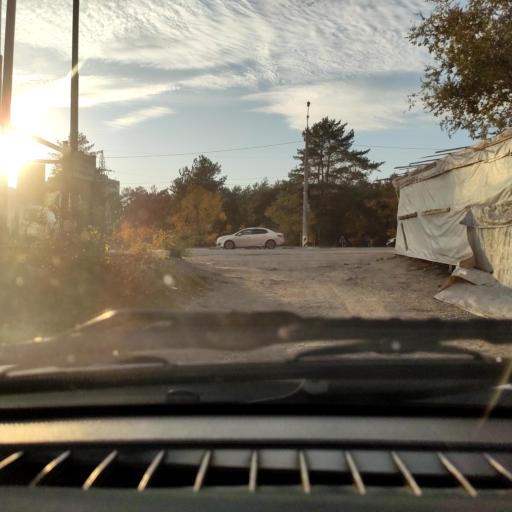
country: RU
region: Samara
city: Zhigulevsk
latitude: 53.4879
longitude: 49.4747
